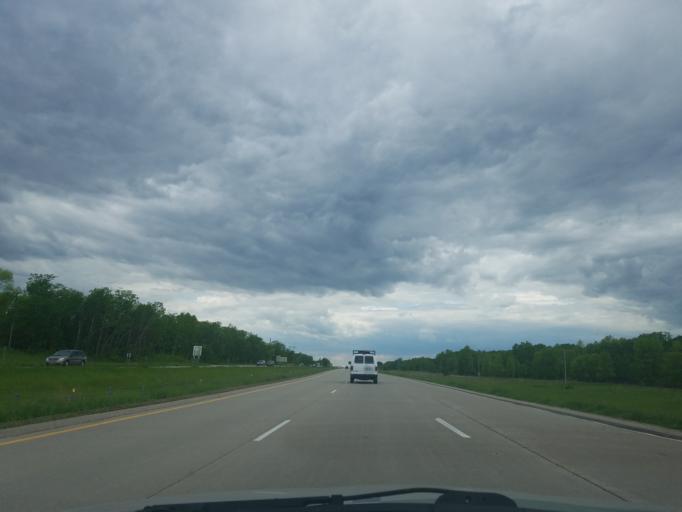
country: US
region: Minnesota
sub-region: Stearns County
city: Sauk Centre
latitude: 45.7480
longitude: -94.9902
